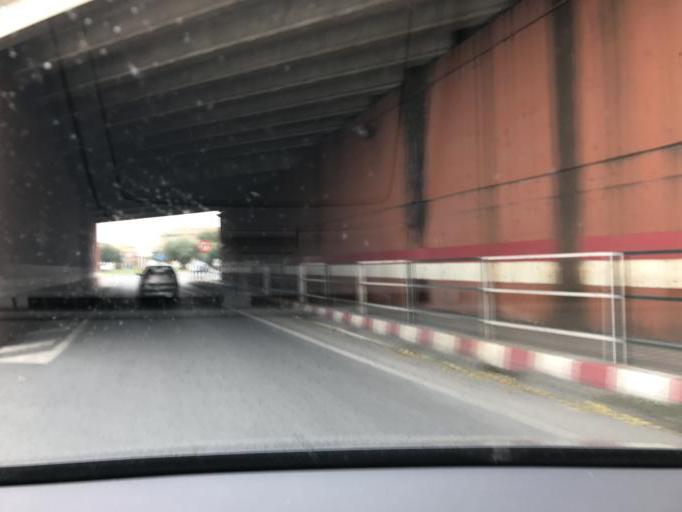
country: ES
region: Andalusia
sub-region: Provincia de Granada
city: Chauchina
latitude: 37.1924
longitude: -3.7246
